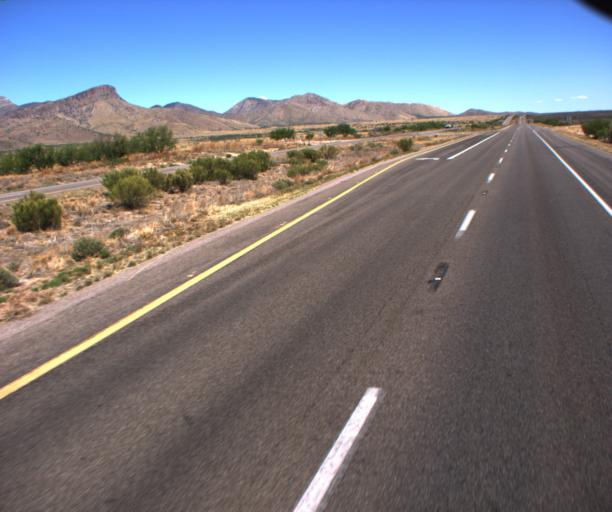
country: US
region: Arizona
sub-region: Cochise County
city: Huachuca City
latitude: 31.7801
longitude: -110.3500
